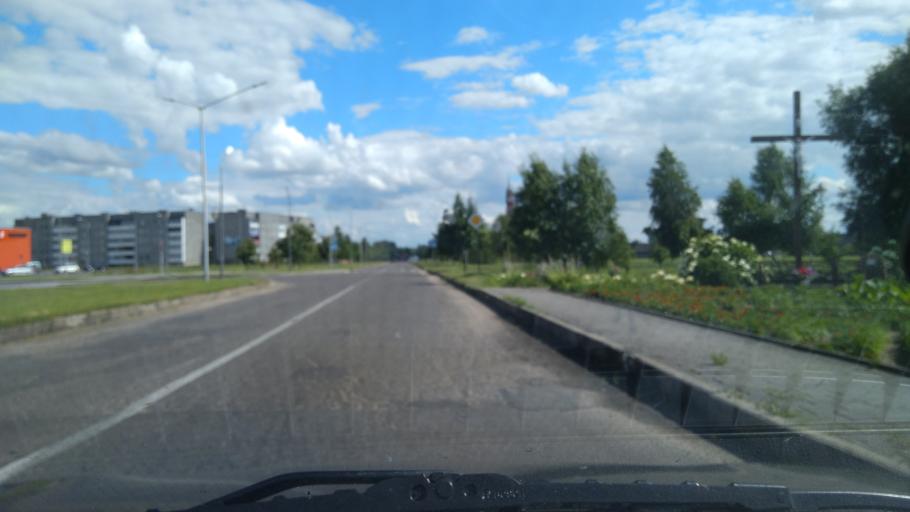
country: BY
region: Grodnenskaya
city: Masty
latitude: 53.4217
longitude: 24.5385
